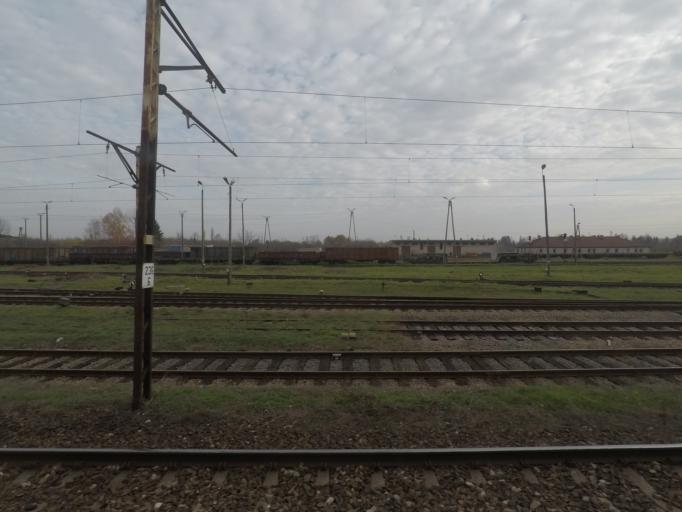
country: PL
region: Subcarpathian Voivodeship
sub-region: Powiat przemyski
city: Zurawica
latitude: 49.8268
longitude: 22.8335
